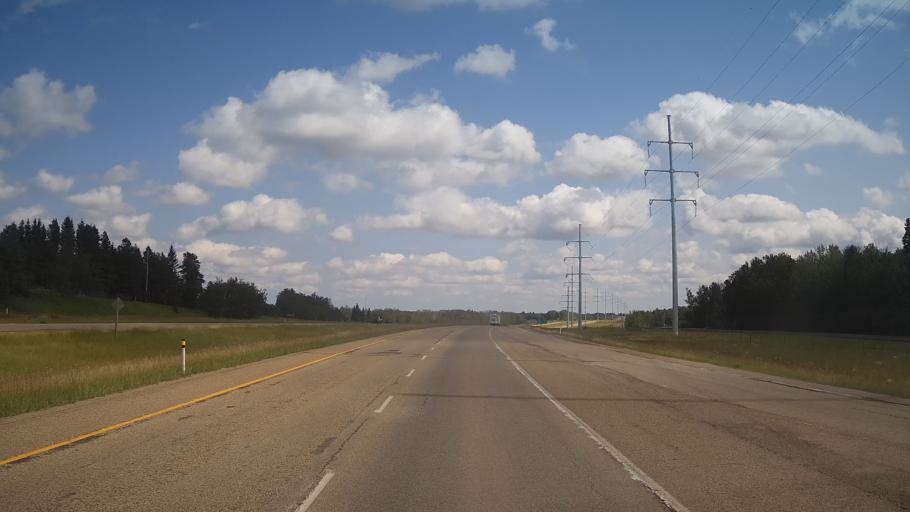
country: CA
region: Alberta
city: Sherwood Park
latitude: 53.4464
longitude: -113.2423
